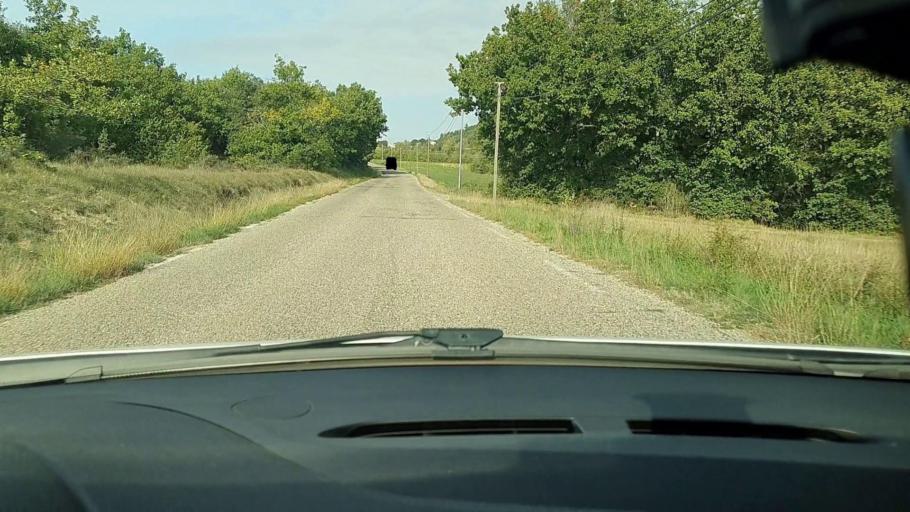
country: FR
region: Languedoc-Roussillon
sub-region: Departement du Gard
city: Goudargues
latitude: 44.1429
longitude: 4.3903
